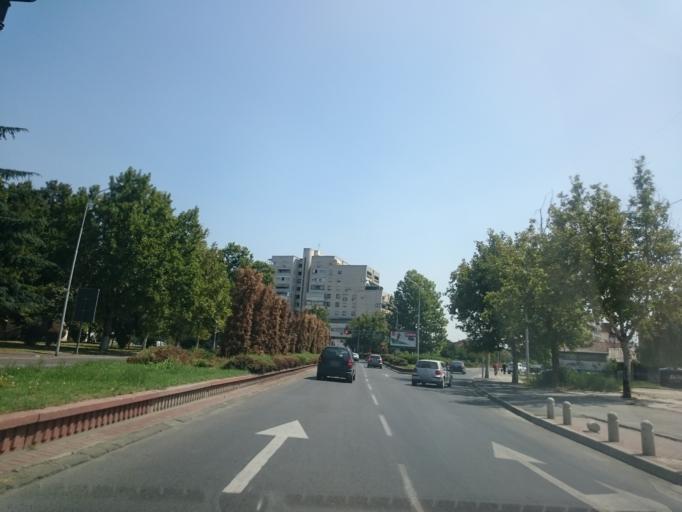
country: MK
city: Krushopek
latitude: 42.0072
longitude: 21.3660
